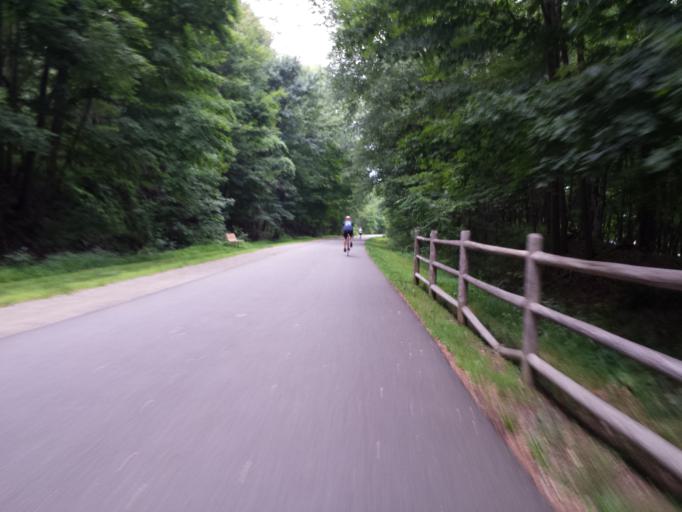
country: US
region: New York
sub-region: Dutchess County
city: Myers Corner
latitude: 41.6280
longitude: -73.8556
